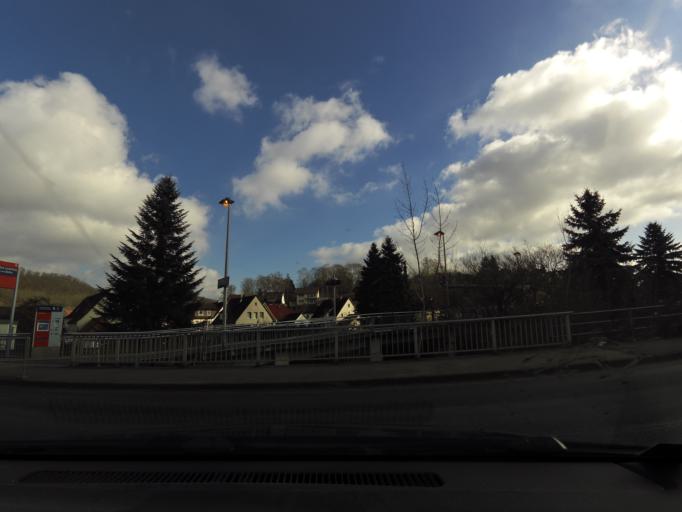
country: DE
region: Lower Saxony
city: Bad Lauterberg im Harz
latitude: 51.6185
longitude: 10.4150
